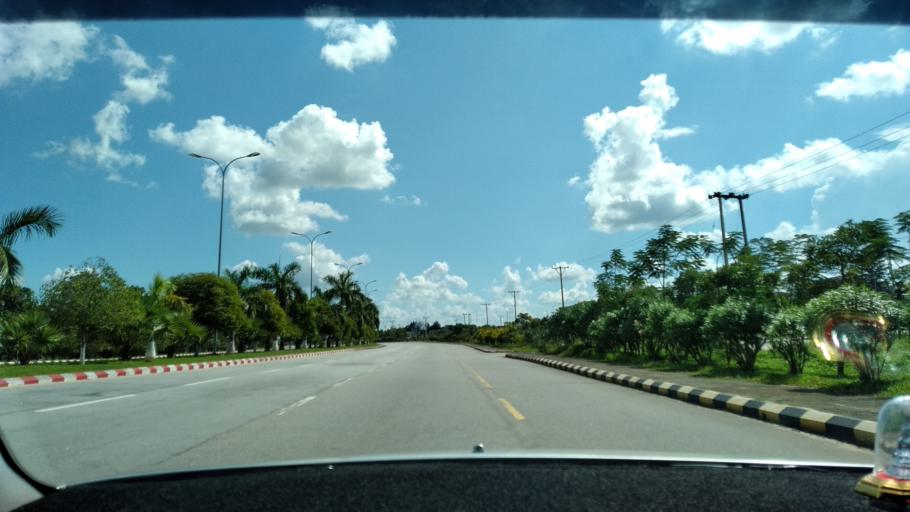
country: MM
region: Mandalay
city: Nay Pyi Taw
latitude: 19.7802
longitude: 96.1434
